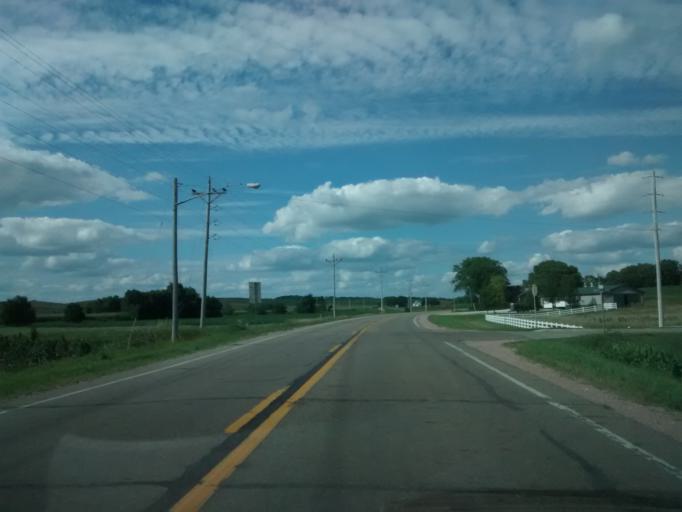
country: US
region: Iowa
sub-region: Woodbury County
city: Moville
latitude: 42.4962
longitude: -96.0719
